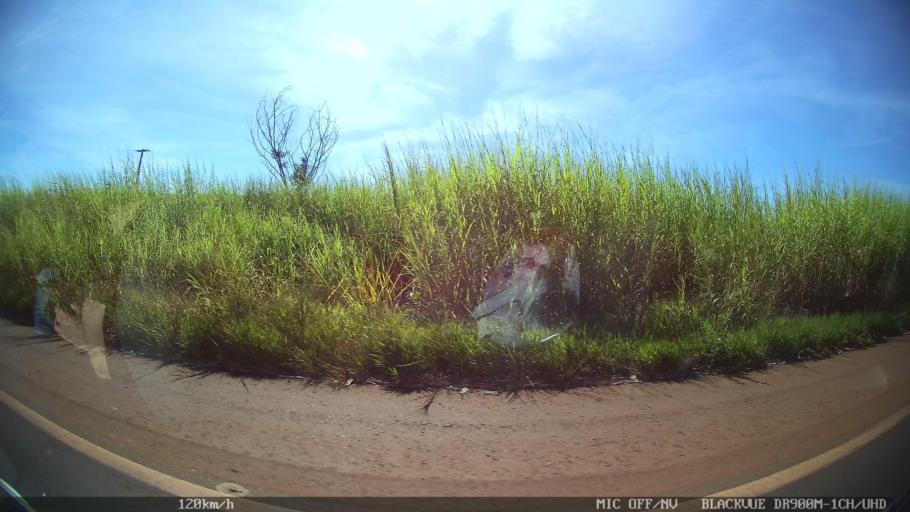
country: BR
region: Sao Paulo
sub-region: Sao Joaquim Da Barra
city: Sao Joaquim da Barra
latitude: -20.5485
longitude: -47.7579
